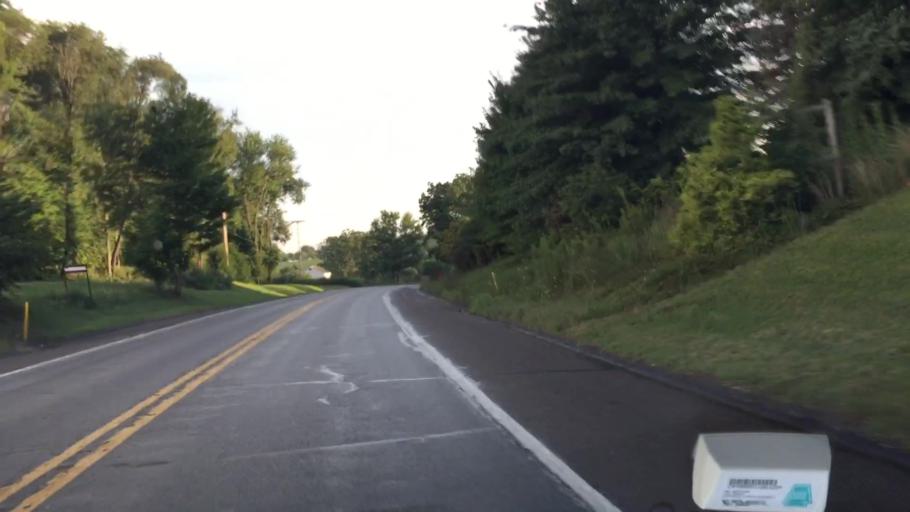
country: US
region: Pennsylvania
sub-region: Butler County
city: Meridian
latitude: 40.8156
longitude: -80.0105
